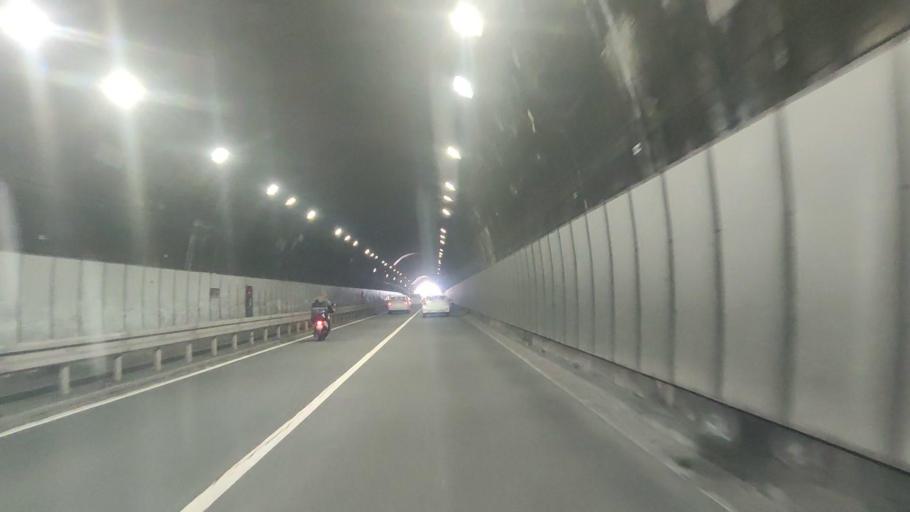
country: JP
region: Oita
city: Oita
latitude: 33.2200
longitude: 131.5948
